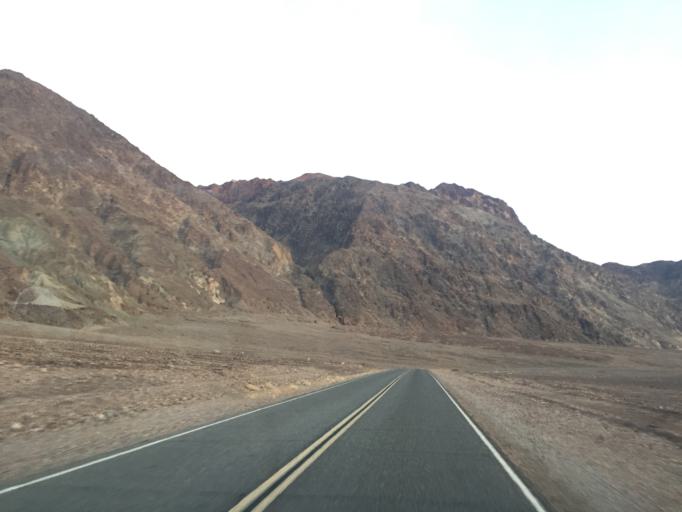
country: US
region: Nevada
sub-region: Nye County
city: Beatty
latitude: 36.1911
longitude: -116.7709
